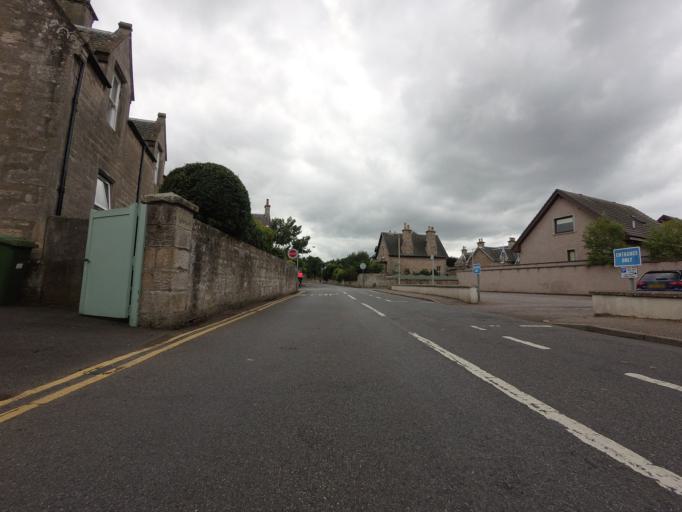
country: GB
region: Scotland
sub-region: Highland
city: Nairn
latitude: 57.5824
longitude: -3.8726
